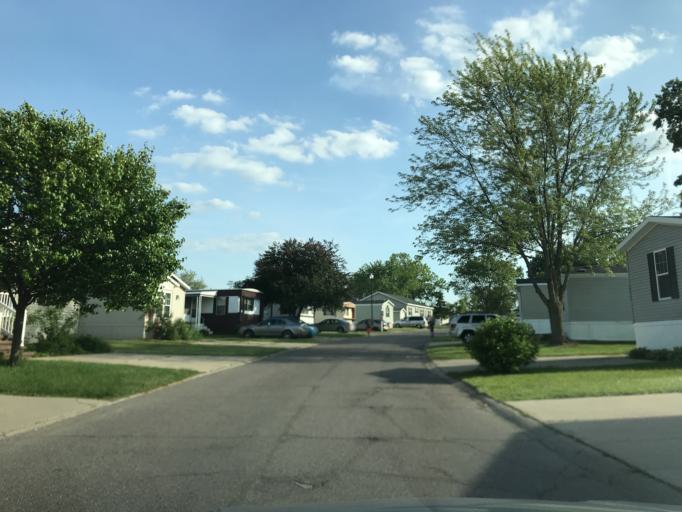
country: US
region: Michigan
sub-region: Oakland County
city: Walled Lake
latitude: 42.5128
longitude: -83.4596
